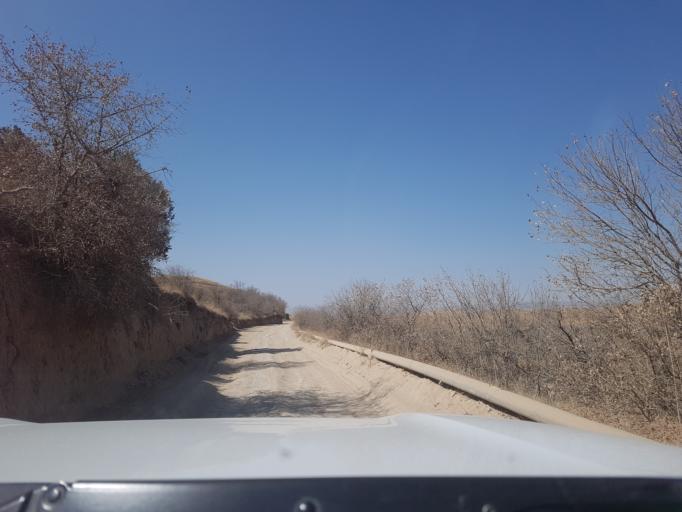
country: TM
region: Ahal
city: Baharly
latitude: 38.2758
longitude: 56.9089
